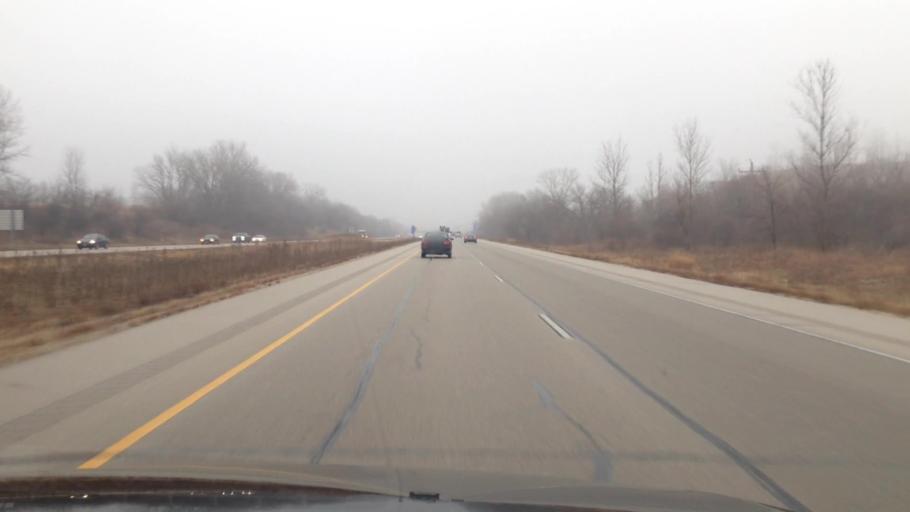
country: US
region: Wisconsin
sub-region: Waukesha County
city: Muskego
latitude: 42.9296
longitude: -88.1743
